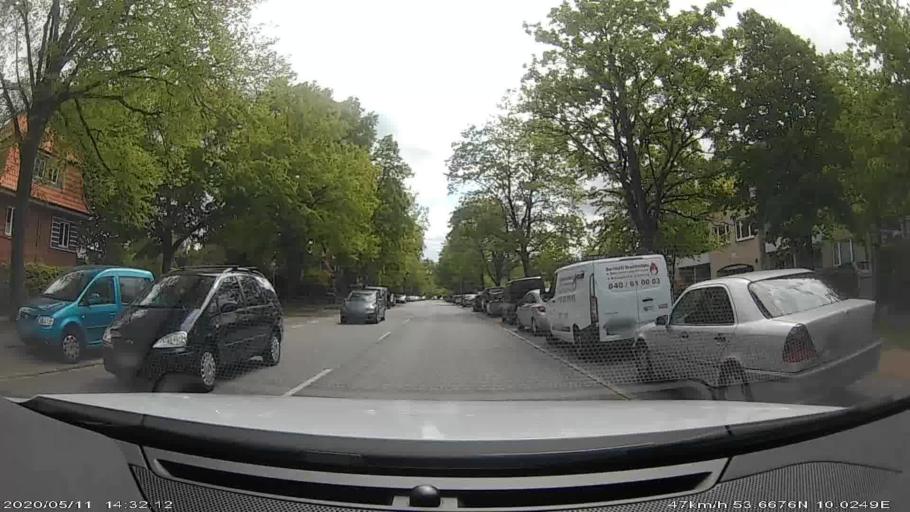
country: DE
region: Hamburg
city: Langenhorn
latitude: 53.6583
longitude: 10.0202
